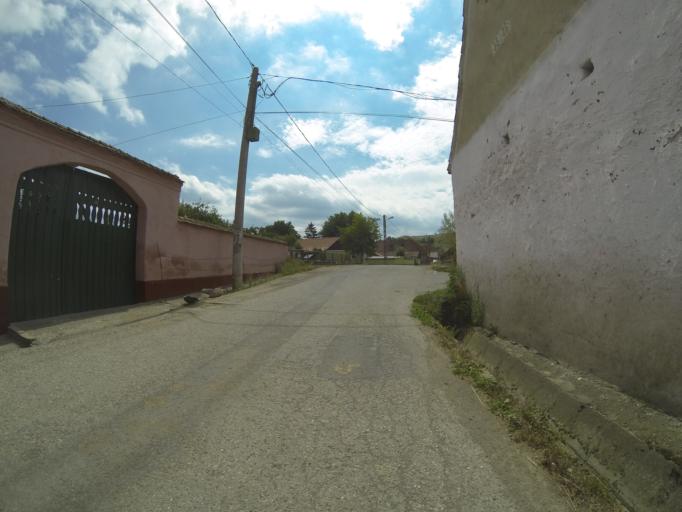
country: RO
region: Brasov
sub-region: Comuna Hoghiz
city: Hoghiz
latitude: 45.9808
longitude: 25.3565
